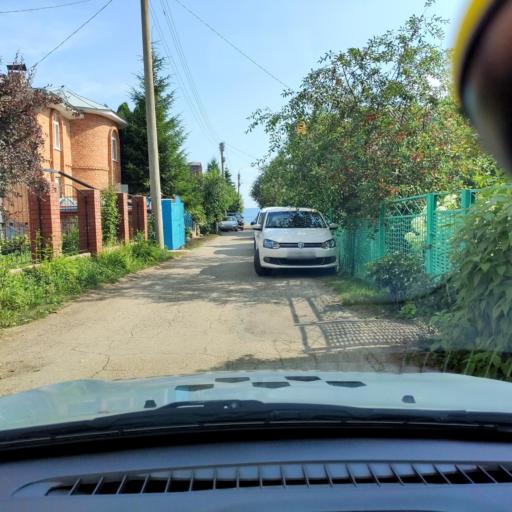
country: RU
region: Samara
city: Podstepki
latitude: 53.5039
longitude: 49.1440
